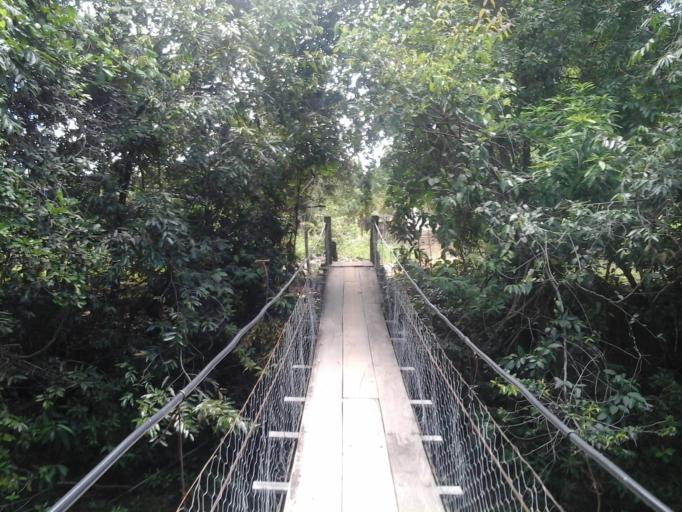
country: BR
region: Goias
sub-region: Pirenopolis
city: Pirenopolis
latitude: -15.7325
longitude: -49.0348
